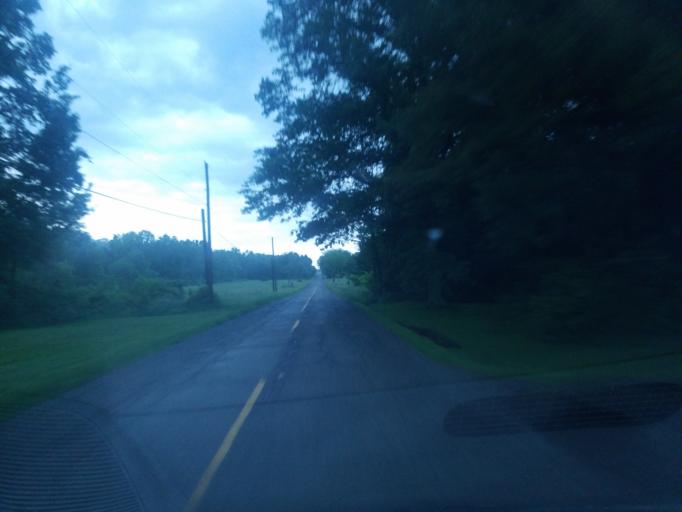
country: US
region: Ohio
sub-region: Mahoning County
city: Canfield
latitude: 40.9728
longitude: -80.7880
